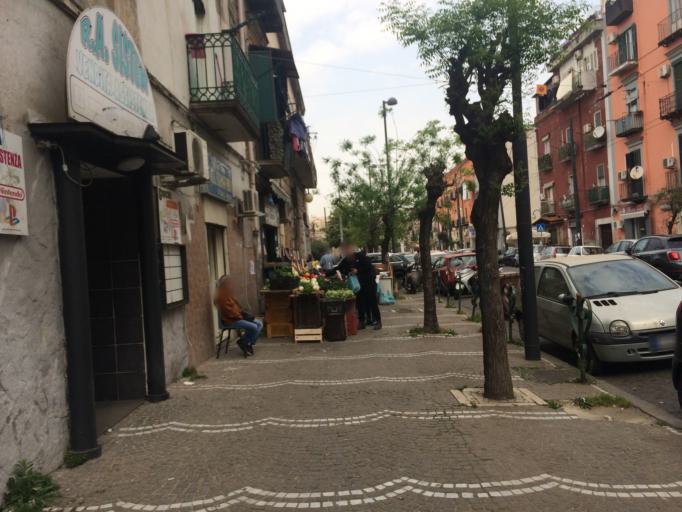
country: IT
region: Campania
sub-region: Provincia di Napoli
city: San Giorgio a Cremano
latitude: 40.8336
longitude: 14.3066
